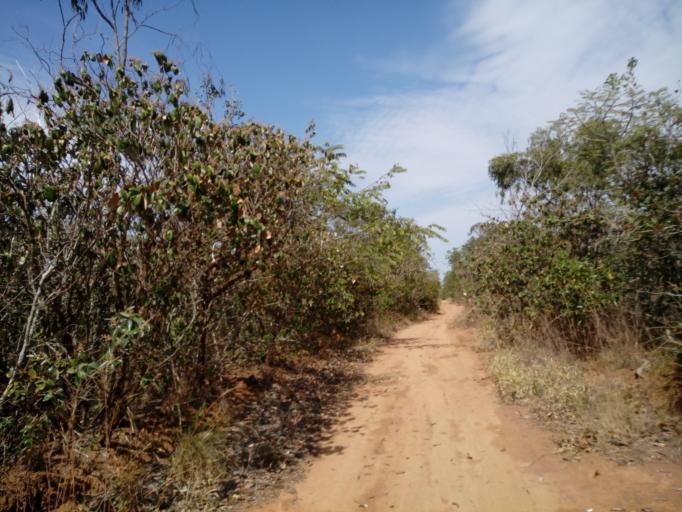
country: BR
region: Sao Paulo
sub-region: Sao Carlos
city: Sao Carlos
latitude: -21.9716
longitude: -47.8810
